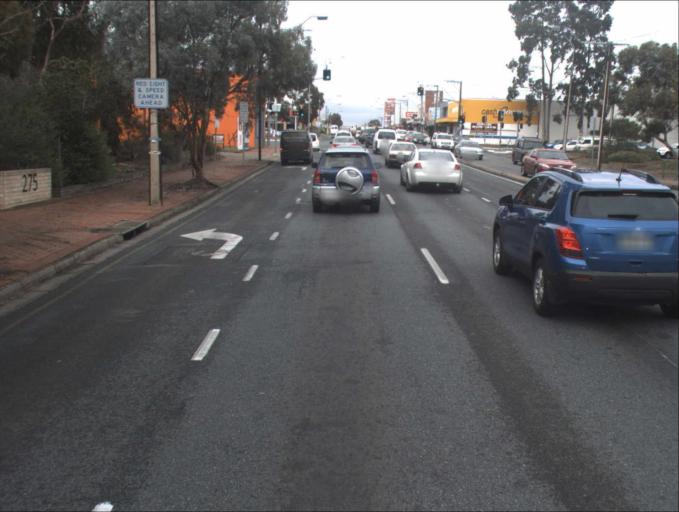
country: AU
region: South Australia
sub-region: Prospect
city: Prospect
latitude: -34.8728
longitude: 138.6020
